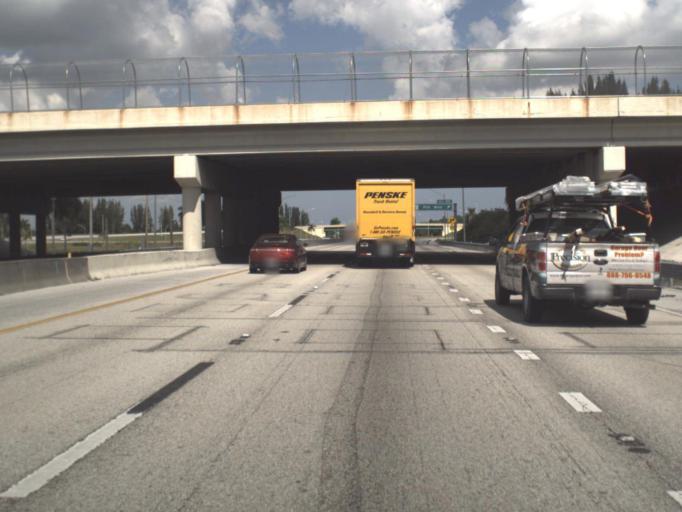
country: US
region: Florida
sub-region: Palm Beach County
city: Palm Beach Gardens
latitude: 26.8385
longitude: -80.1300
